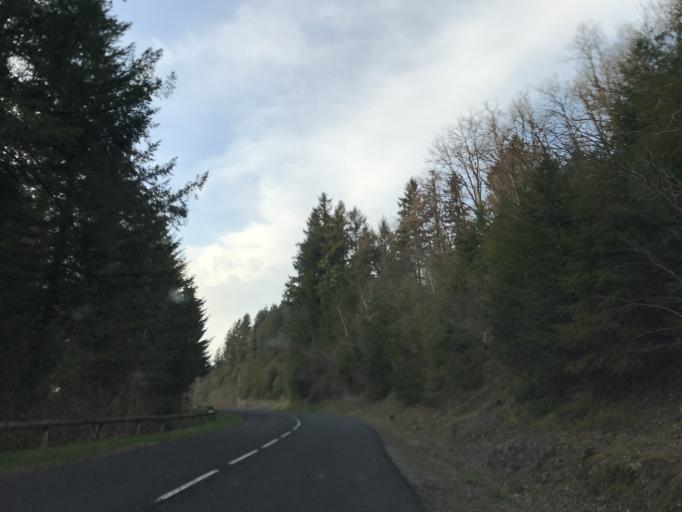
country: FR
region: Auvergne
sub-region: Departement du Puy-de-Dome
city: La Monnerie-le-Montel
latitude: 45.8683
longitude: 3.5898
